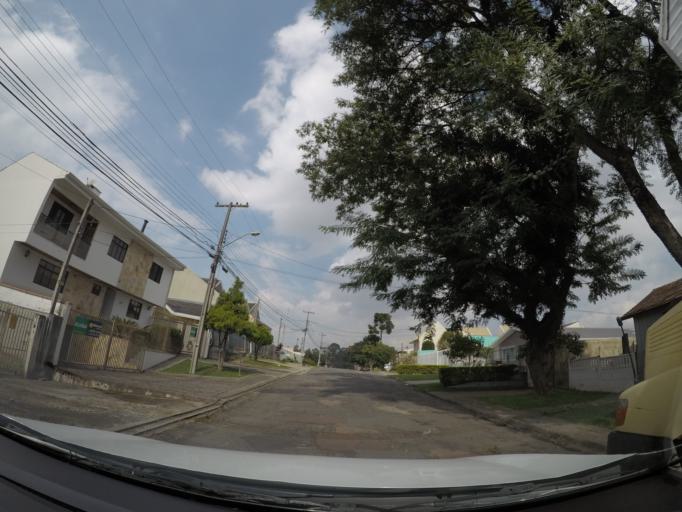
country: BR
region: Parana
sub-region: Sao Jose Dos Pinhais
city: Sao Jose dos Pinhais
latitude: -25.5017
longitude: -49.2414
